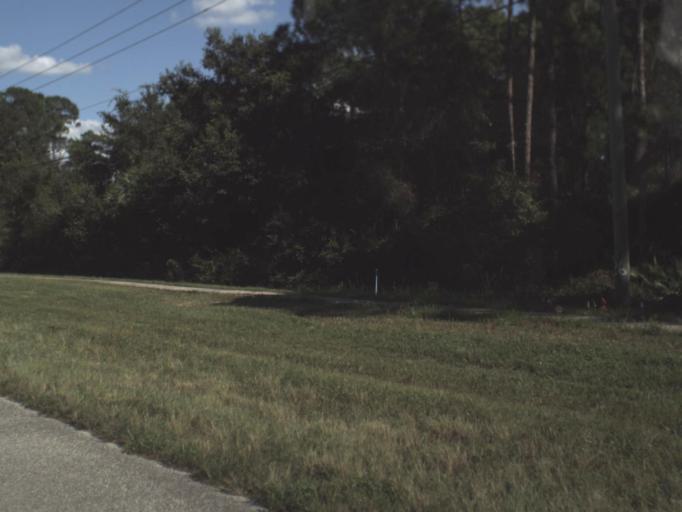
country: US
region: Florida
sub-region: Sarasota County
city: North Port
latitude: 27.0024
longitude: -82.1766
